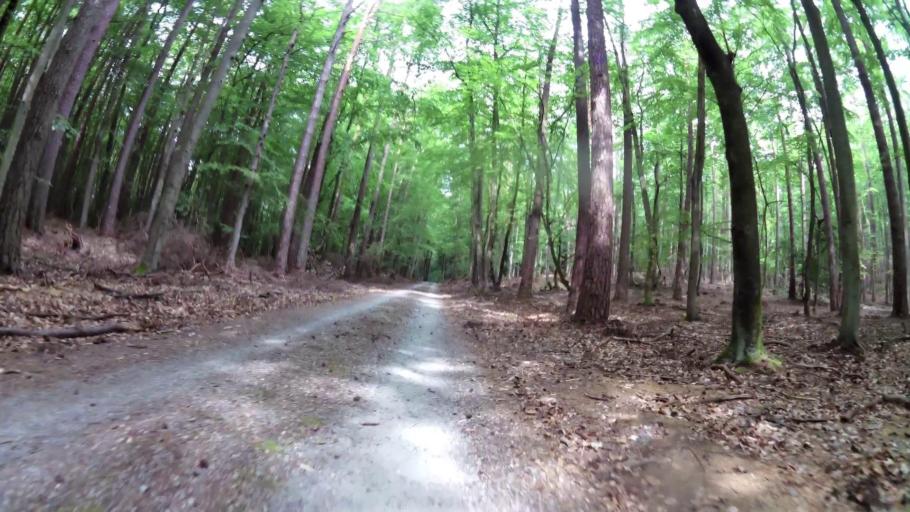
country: PL
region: West Pomeranian Voivodeship
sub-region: Powiat kamienski
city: Miedzyzdroje
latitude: 53.9464
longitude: 14.5168
